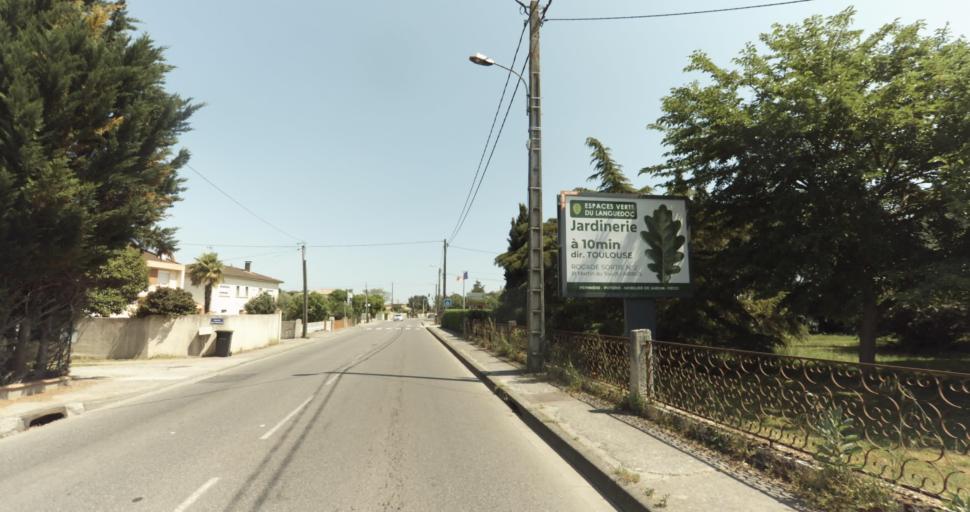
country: FR
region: Midi-Pyrenees
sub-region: Departement de la Haute-Garonne
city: La Salvetat-Saint-Gilles
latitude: 43.5719
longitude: 1.2691
